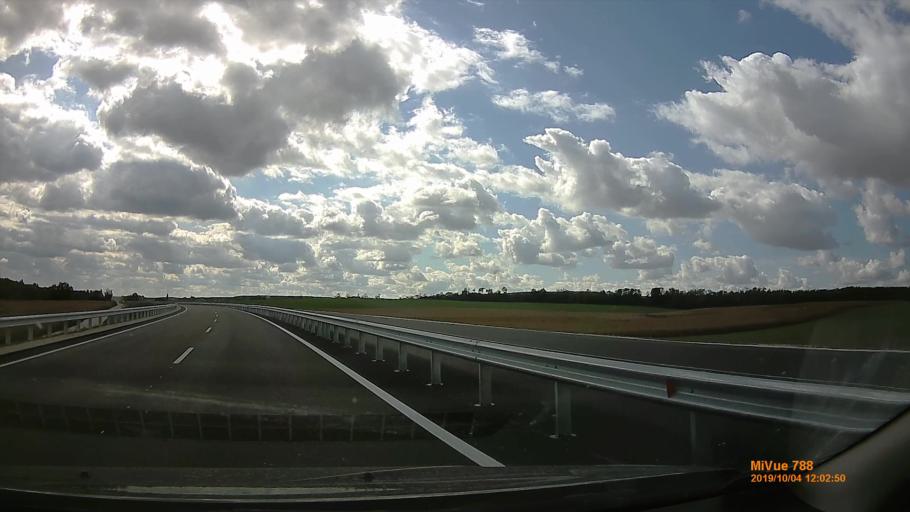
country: HU
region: Somogy
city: Karad
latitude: 46.5955
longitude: 17.8023
